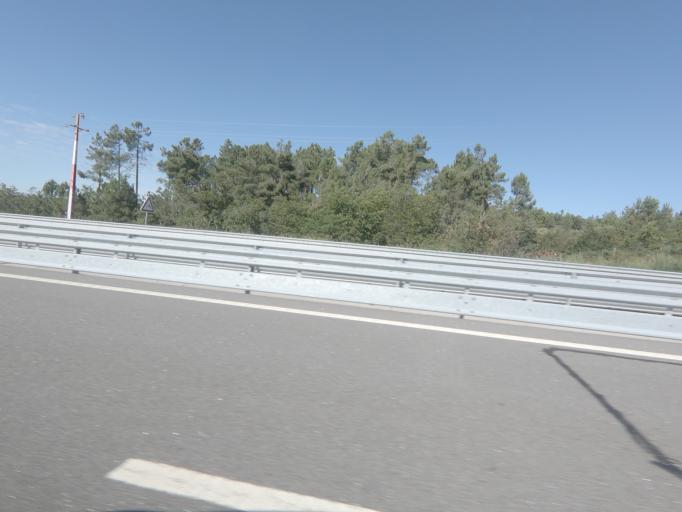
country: PT
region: Vila Real
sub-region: Santa Marta de Penaguiao
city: Santa Marta de Penaguiao
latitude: 41.2713
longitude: -7.8173
